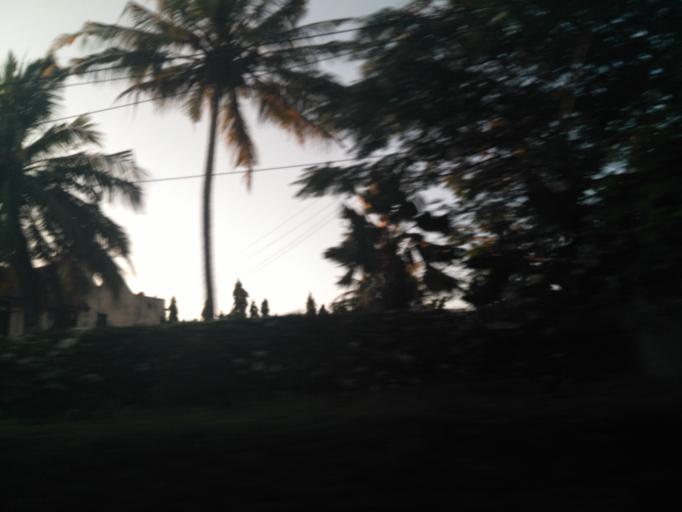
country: TZ
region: Dar es Salaam
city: Magomeni
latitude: -6.7746
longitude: 39.2802
